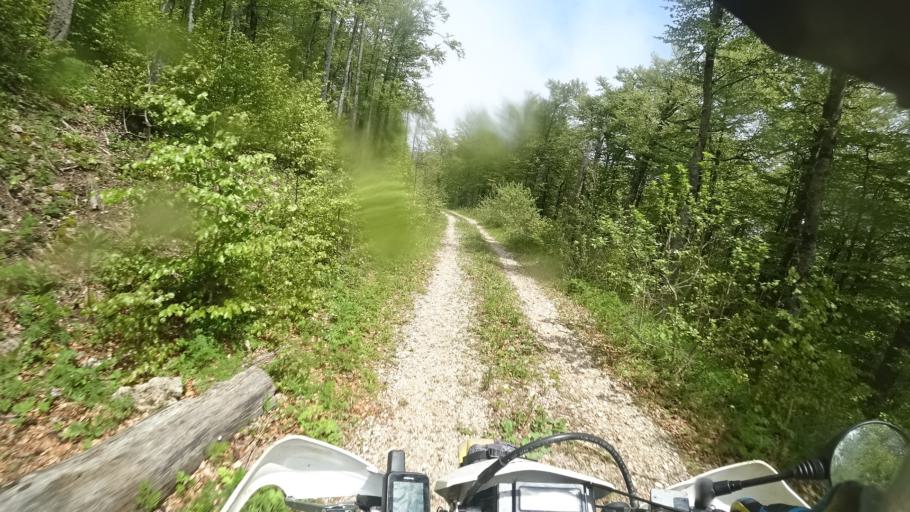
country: BA
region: Federation of Bosnia and Herzegovina
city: Orasac
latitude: 44.5711
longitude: 15.8767
